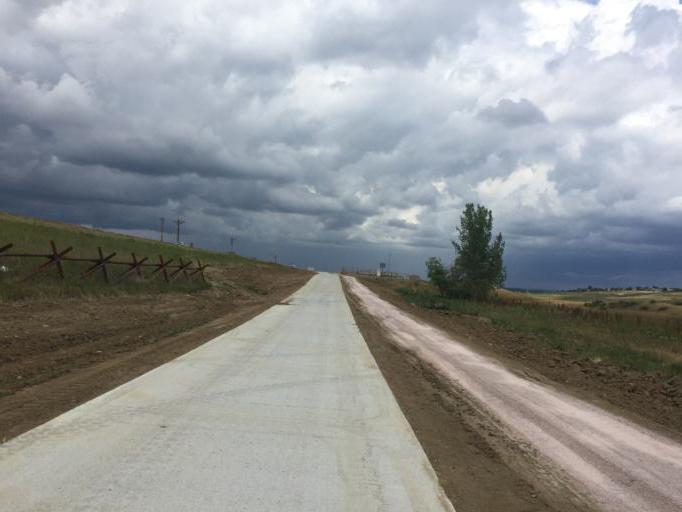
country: US
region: Colorado
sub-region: Larimer County
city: Loveland
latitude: 40.4787
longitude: -105.0962
